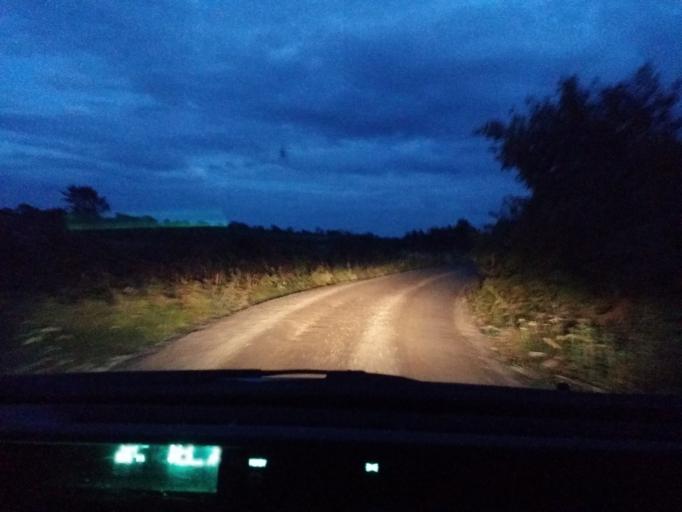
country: SE
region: Kalmar
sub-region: Borgholms Kommun
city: Borgholm
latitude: 57.1285
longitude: 16.9016
